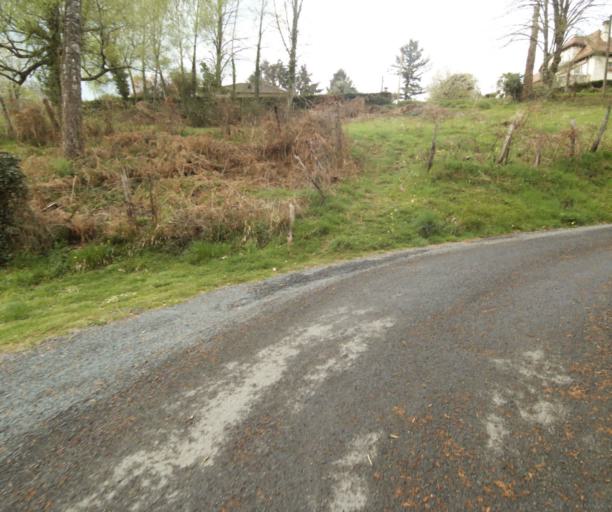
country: FR
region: Limousin
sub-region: Departement de la Correze
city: Tulle
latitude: 45.2834
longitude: 1.7360
